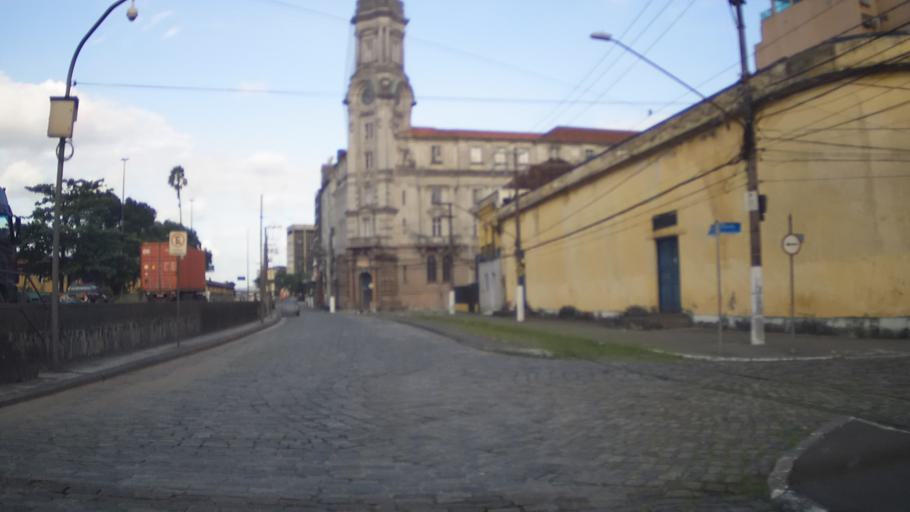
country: BR
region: Sao Paulo
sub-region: Santos
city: Santos
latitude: -23.9316
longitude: -46.3311
